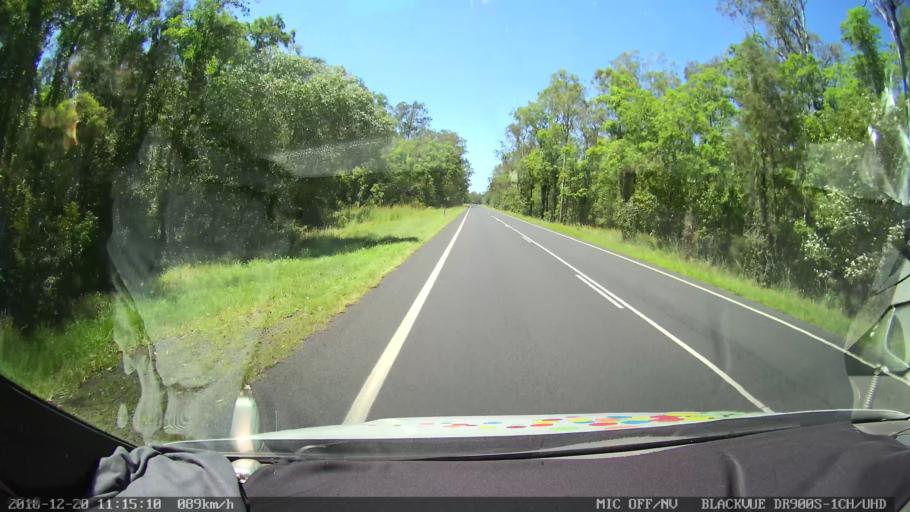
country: AU
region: New South Wales
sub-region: Richmond Valley
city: Casino
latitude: -29.0099
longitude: 153.0070
